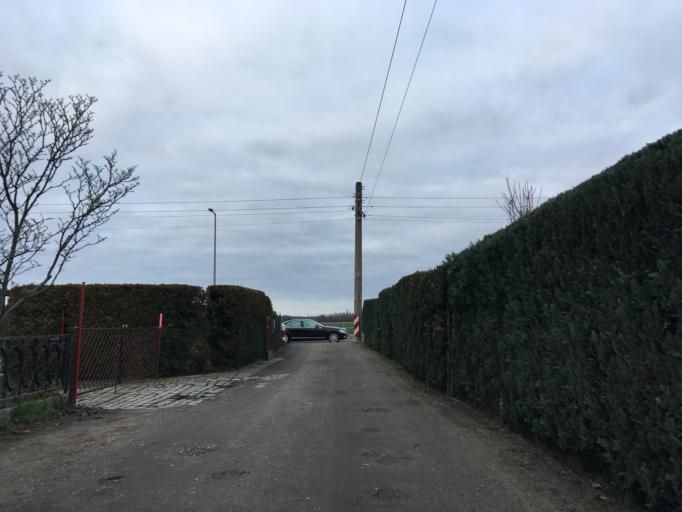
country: DE
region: Berlin
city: Buchholz
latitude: 52.6039
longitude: 13.4105
